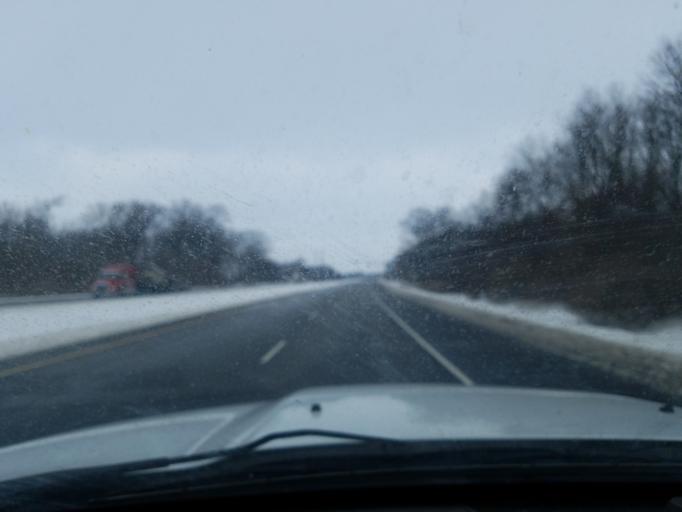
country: US
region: Indiana
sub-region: Marshall County
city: Argos
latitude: 41.2788
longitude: -86.2714
